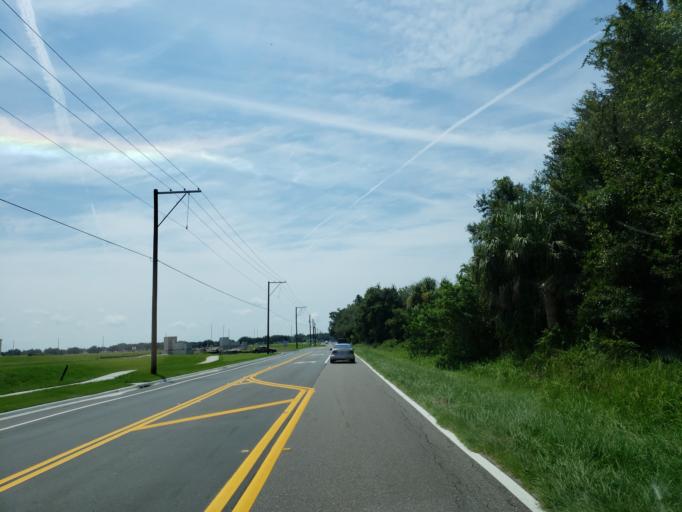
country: US
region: Florida
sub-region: Hillsborough County
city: Riverview
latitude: 27.8413
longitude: -82.3433
